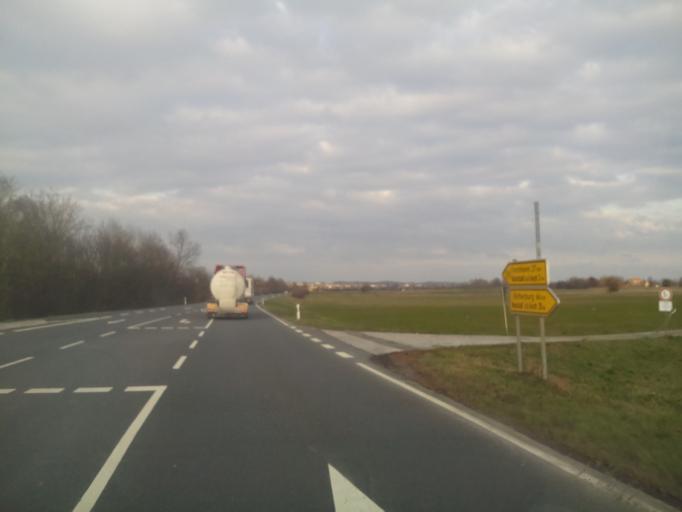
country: DE
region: Bavaria
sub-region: Regierungsbezirk Mittelfranken
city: Lonnerstadt
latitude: 49.6975
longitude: 10.7695
